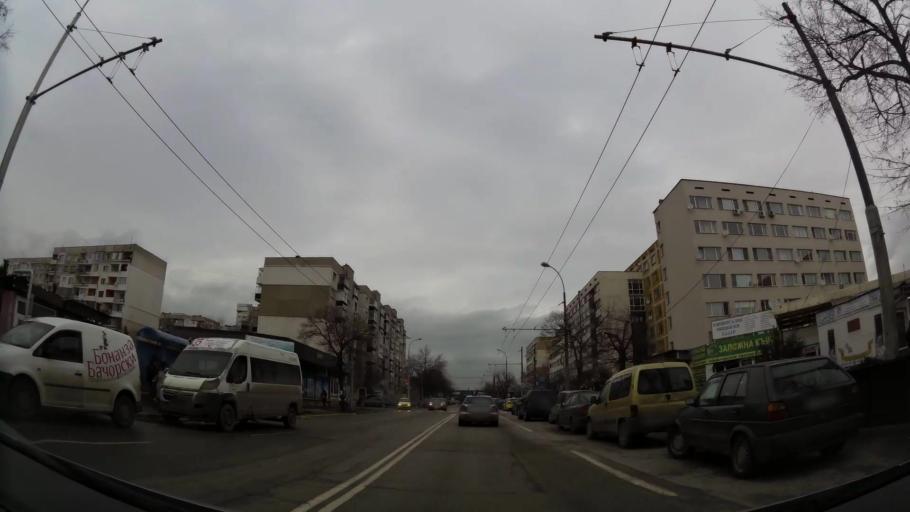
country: BG
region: Sofiya
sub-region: Obshtina Bozhurishte
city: Bozhurishte
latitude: 42.7284
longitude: 23.2497
